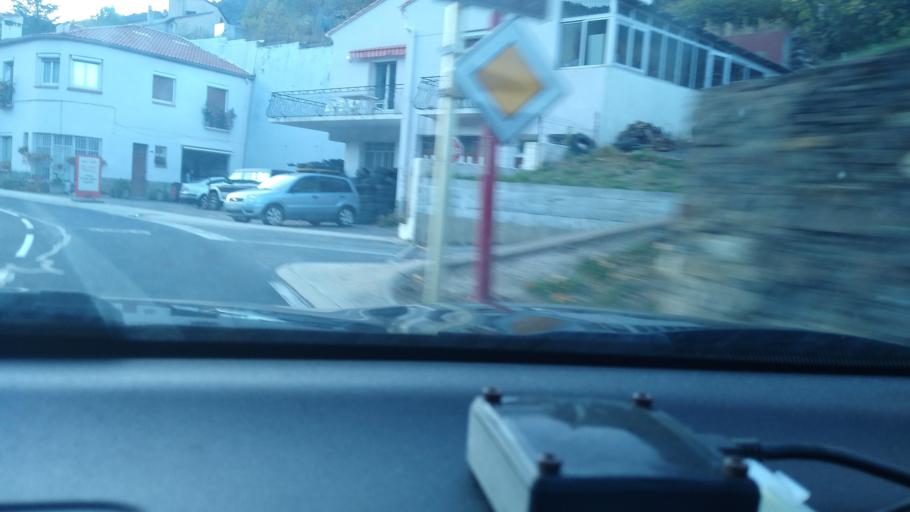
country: FR
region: Languedoc-Roussillon
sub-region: Departement des Pyrenees-Orientales
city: Vernet-les-Bains
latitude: 42.5562
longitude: 2.2767
